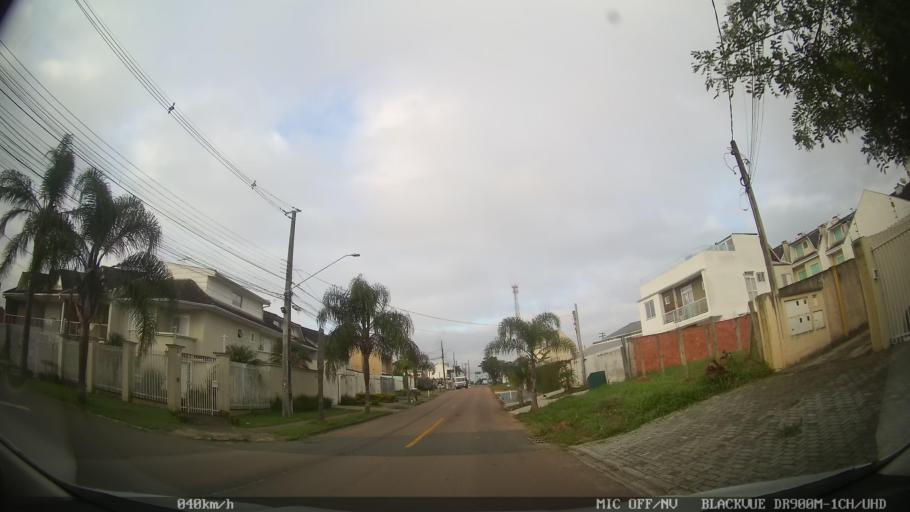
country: BR
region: Parana
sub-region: Almirante Tamandare
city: Almirante Tamandare
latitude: -25.3896
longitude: -49.3374
